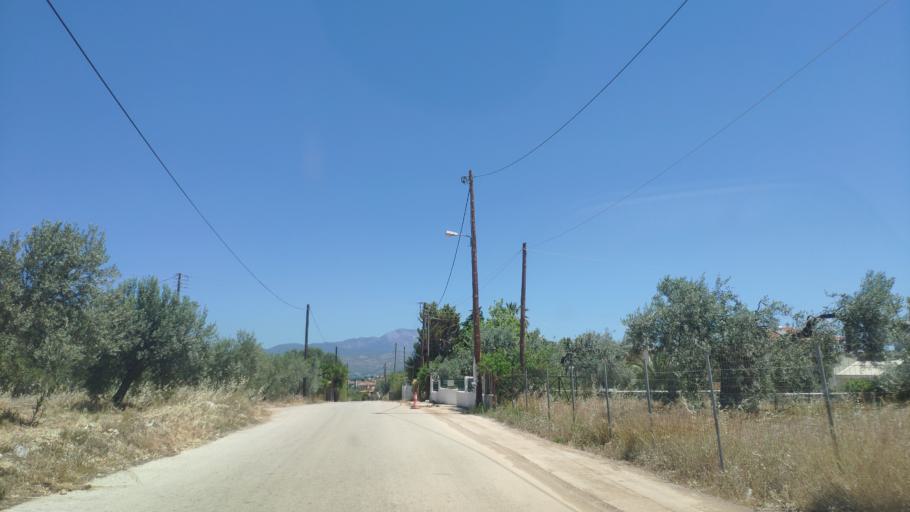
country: GR
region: Peloponnese
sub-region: Nomos Korinthias
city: Loutra Oraias Elenis
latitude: 37.8538
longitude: 22.9877
